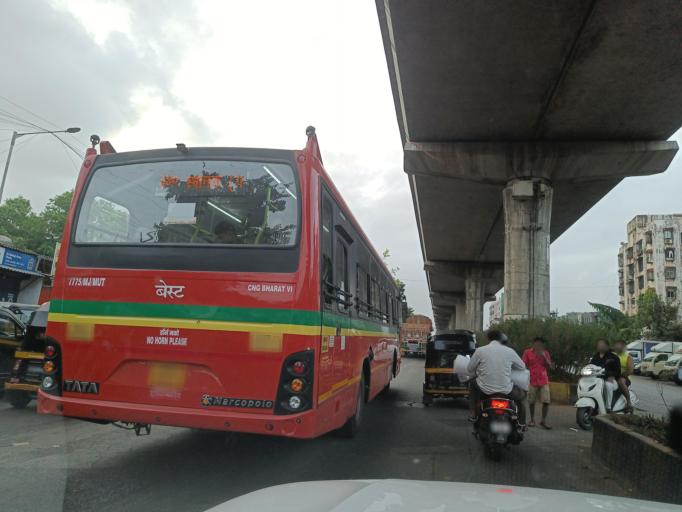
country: IN
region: Maharashtra
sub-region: Mumbai Suburban
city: Powai
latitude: 19.0956
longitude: 72.8961
